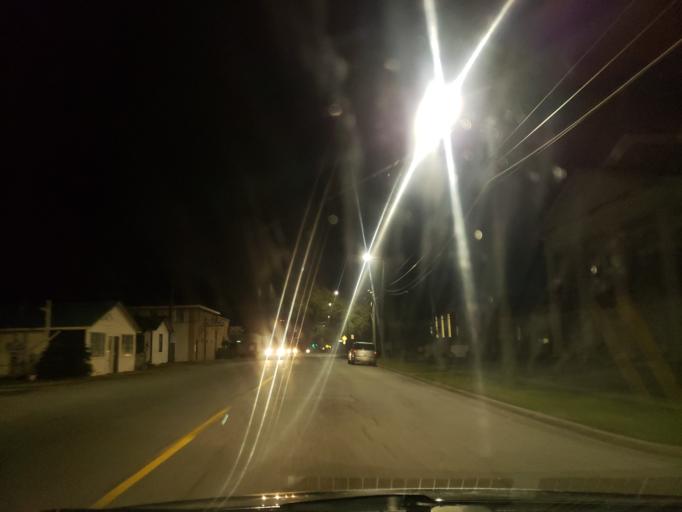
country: US
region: Georgia
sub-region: Chatham County
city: Savannah
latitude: 32.0426
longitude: -81.1061
